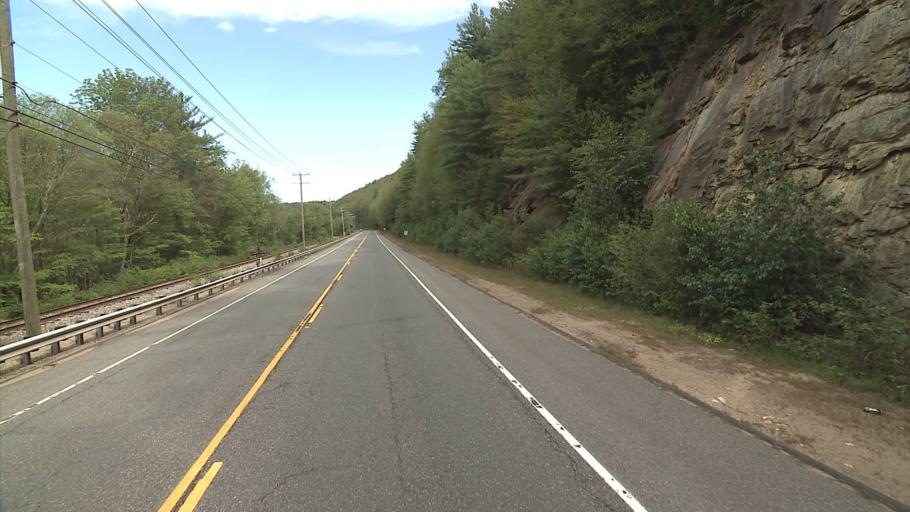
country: US
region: Connecticut
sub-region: Tolland County
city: Stafford Springs
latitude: 41.9144
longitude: -72.2970
